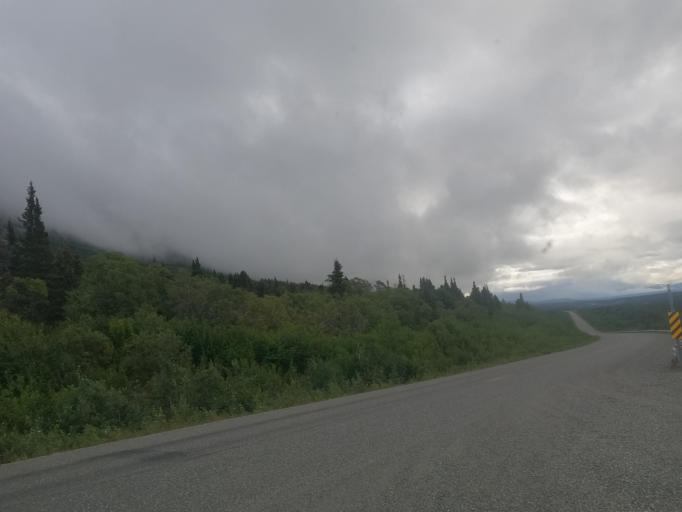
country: CA
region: Yukon
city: Haines Junction
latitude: 60.0391
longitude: -136.8832
